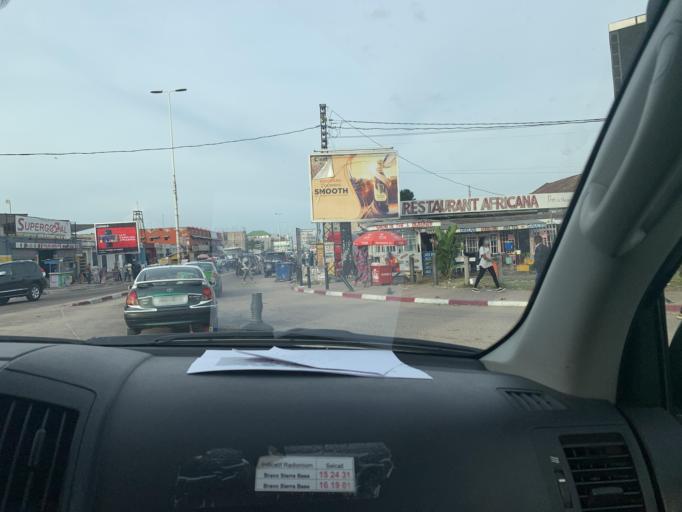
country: CG
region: Brazzaville
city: Brazzaville
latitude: -4.2542
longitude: 15.2737
